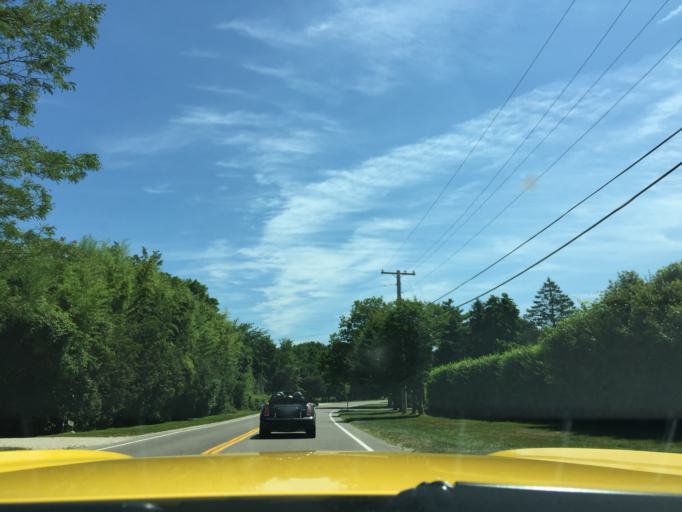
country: US
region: New York
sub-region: Suffolk County
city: Bridgehampton
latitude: 40.9310
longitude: -72.2852
